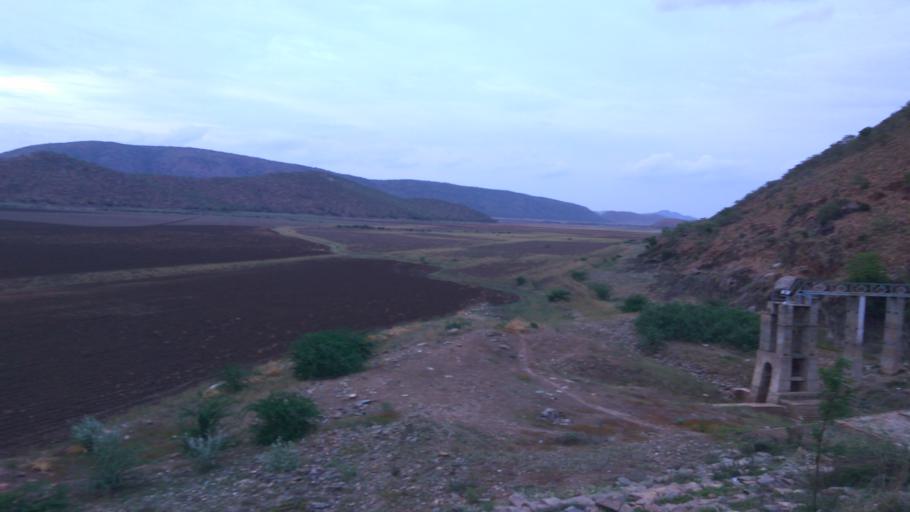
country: IN
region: Andhra Pradesh
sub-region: Prakasam
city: Cumbum
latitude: 15.5774
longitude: 79.0820
